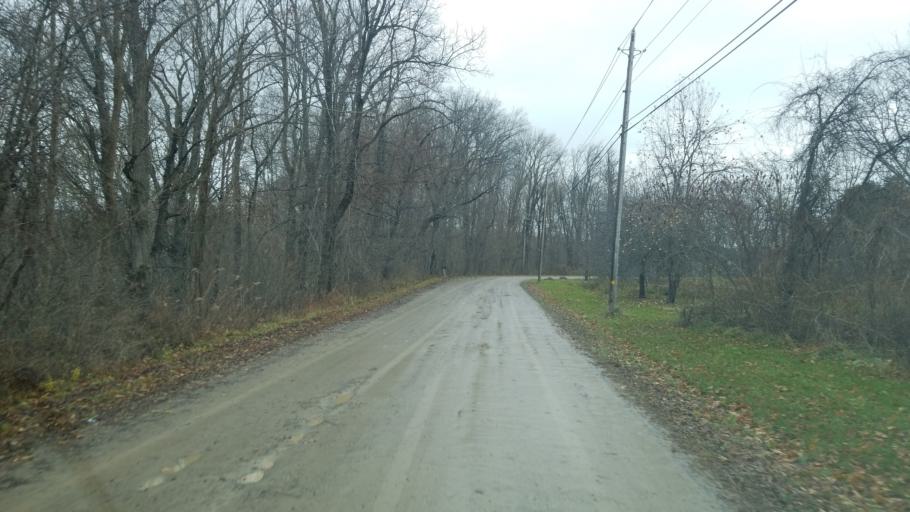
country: US
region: Ohio
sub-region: Ashtabula County
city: Conneaut
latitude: 41.9184
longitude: -80.6043
